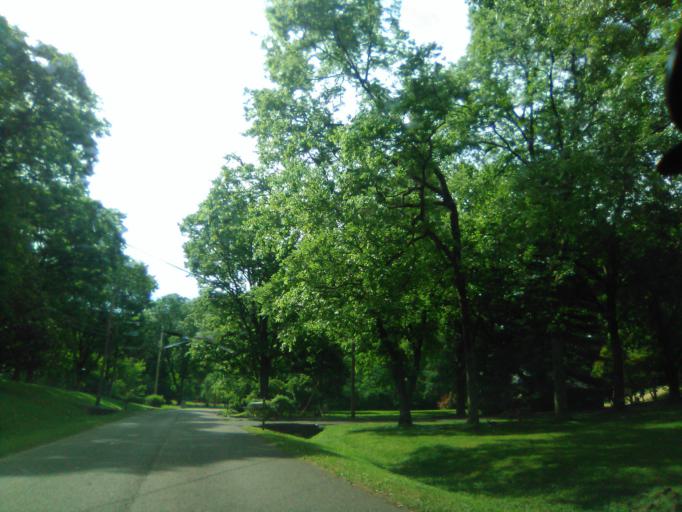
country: US
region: Tennessee
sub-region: Davidson County
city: Belle Meade
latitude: 36.1039
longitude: -86.9029
